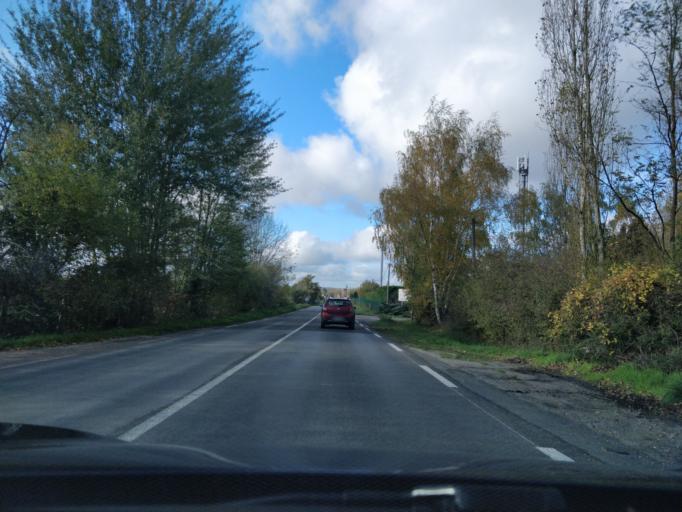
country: FR
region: Ile-de-France
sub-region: Departement de l'Essonne
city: Bruyeres-le-Chatel
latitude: 48.6106
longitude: 2.1772
